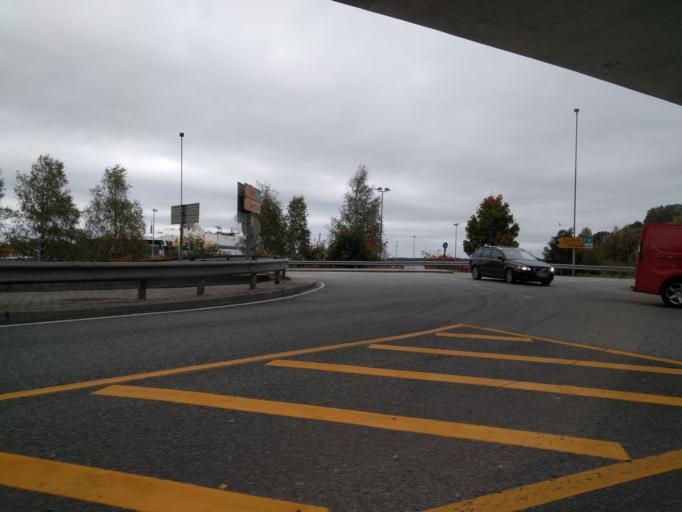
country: NO
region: Vest-Agder
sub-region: Kristiansand
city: Kristiansand
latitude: 58.1452
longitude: 7.9823
